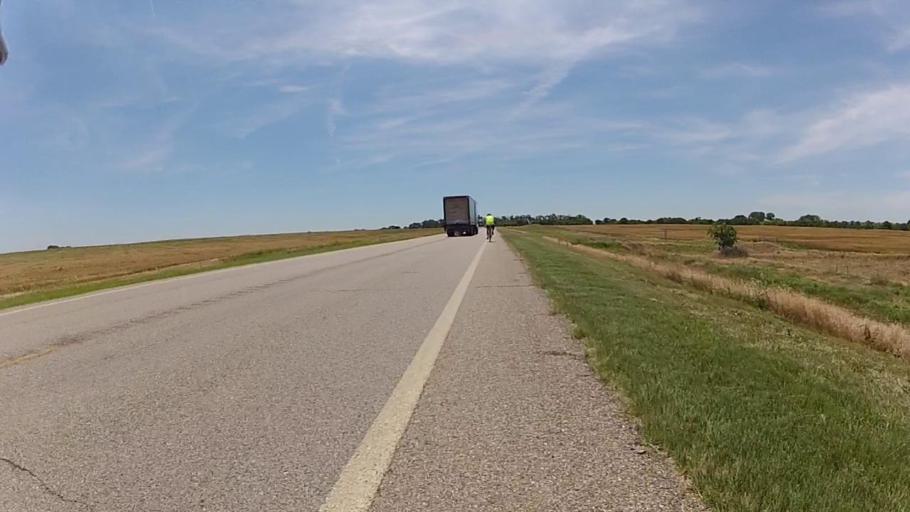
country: US
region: Kansas
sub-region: Barber County
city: Medicine Lodge
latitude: 37.2605
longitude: -98.5280
